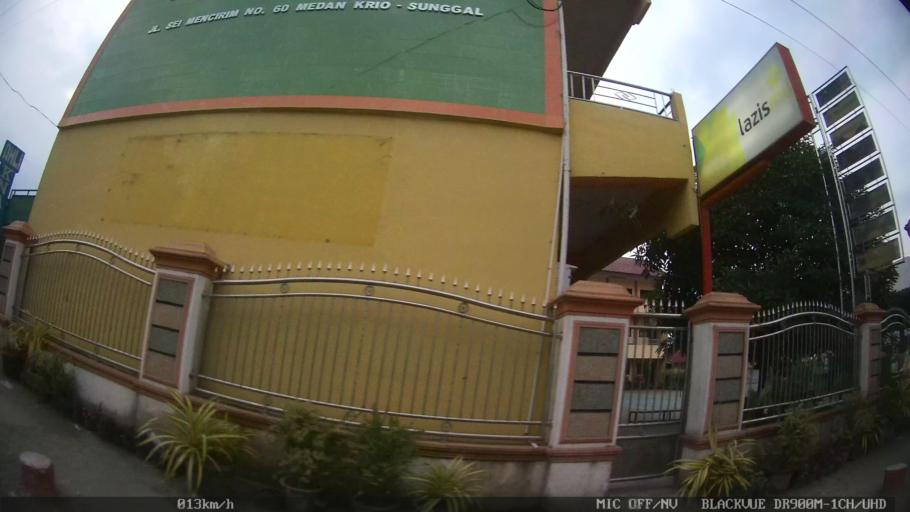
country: ID
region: North Sumatra
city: Sunggal
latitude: 3.5778
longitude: 98.5888
